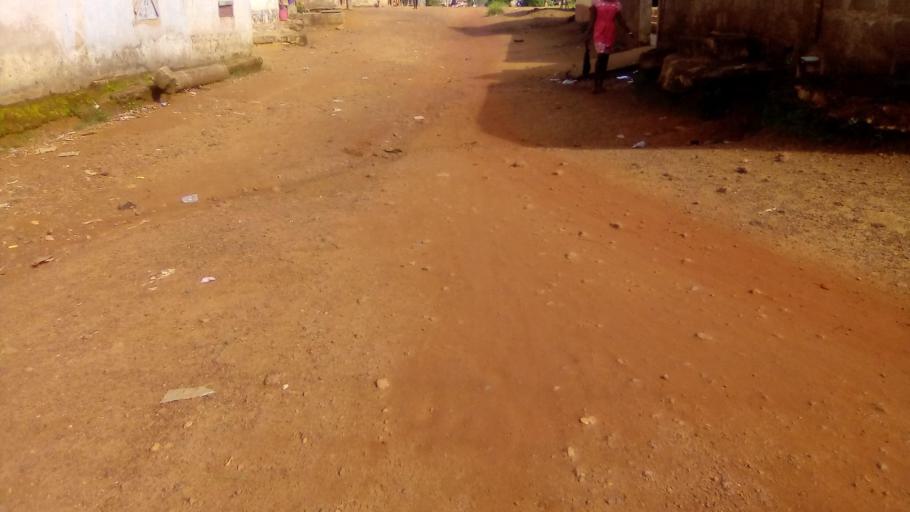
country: SL
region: Southern Province
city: Bo
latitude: 7.9724
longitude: -11.7311
